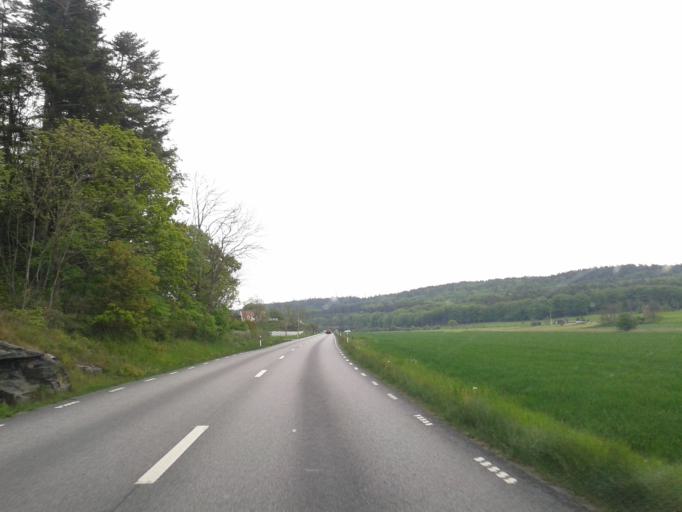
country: SE
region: Vaestra Goetaland
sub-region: Kungalvs Kommun
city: Kode
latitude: 57.8909
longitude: 11.7679
